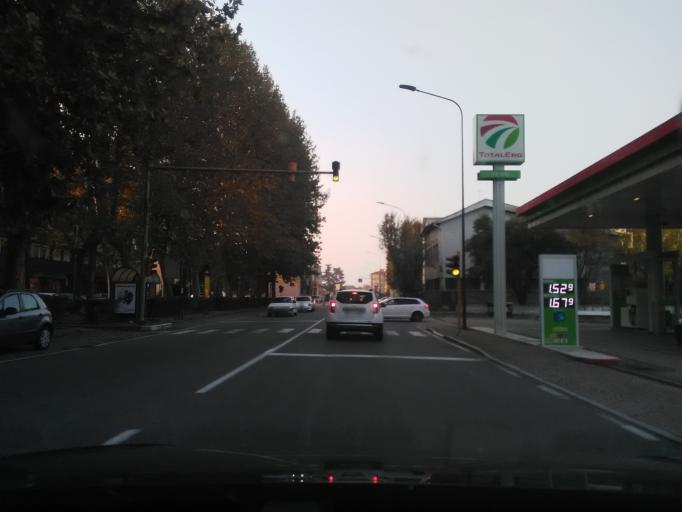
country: IT
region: Piedmont
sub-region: Provincia di Alessandria
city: Casale Monferrato
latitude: 45.1455
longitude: 8.4457
